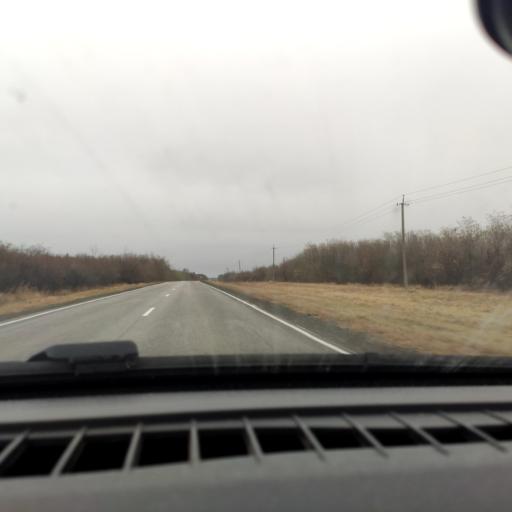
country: RU
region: Voronezj
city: Uryv-Pokrovka
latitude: 51.0956
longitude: 39.0115
